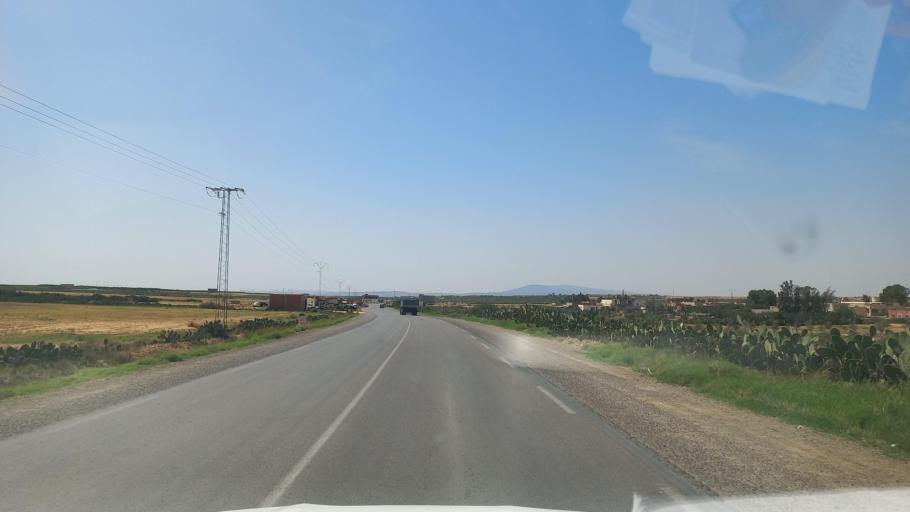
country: TN
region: Al Qasrayn
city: Sbiba
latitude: 35.3645
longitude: 9.0952
